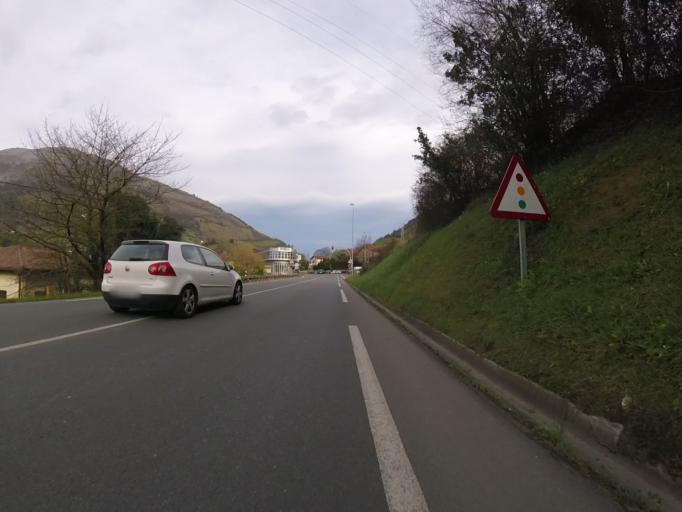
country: ES
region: Basque Country
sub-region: Provincia de Guipuzcoa
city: Azpeitia
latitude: 43.1830
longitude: -2.2603
